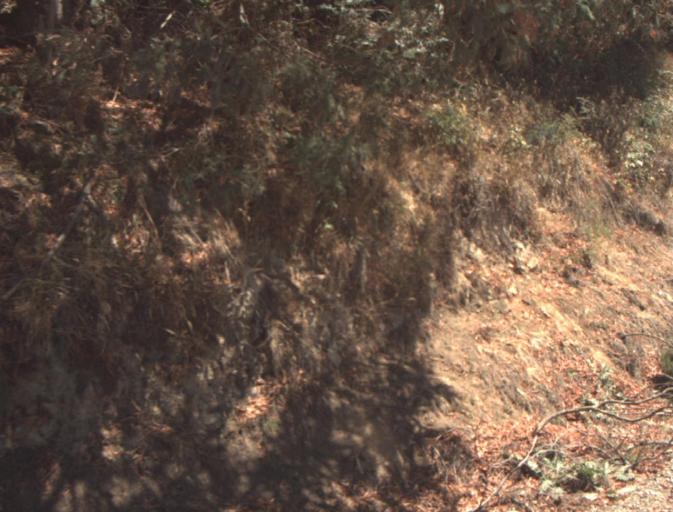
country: AU
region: Tasmania
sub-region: Dorset
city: Scottsdale
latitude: -41.3058
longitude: 147.3681
